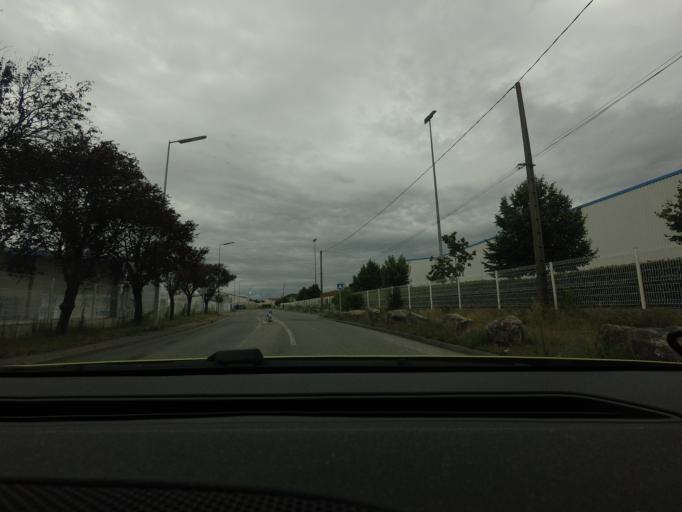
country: FR
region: Midi-Pyrenees
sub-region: Departement de la Haute-Garonne
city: Tournefeuille
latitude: 43.6012
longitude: 1.3019
